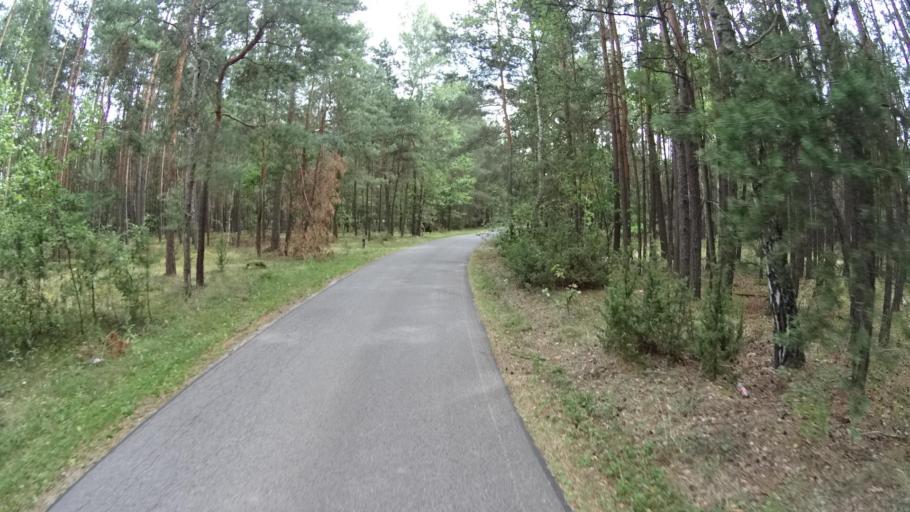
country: PL
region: Masovian Voivodeship
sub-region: Powiat bialobrzeski
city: Bialobrzegi
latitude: 51.6373
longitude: 20.9026
